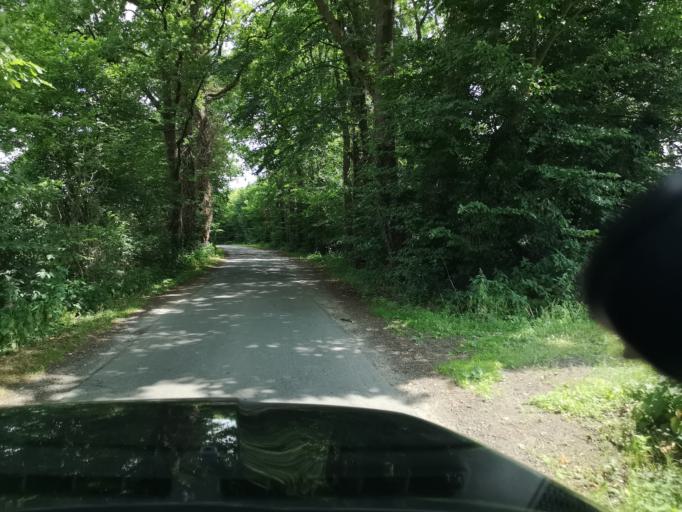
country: DE
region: North Rhine-Westphalia
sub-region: Regierungsbezirk Munster
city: Rhede
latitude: 51.8574
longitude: 6.6860
